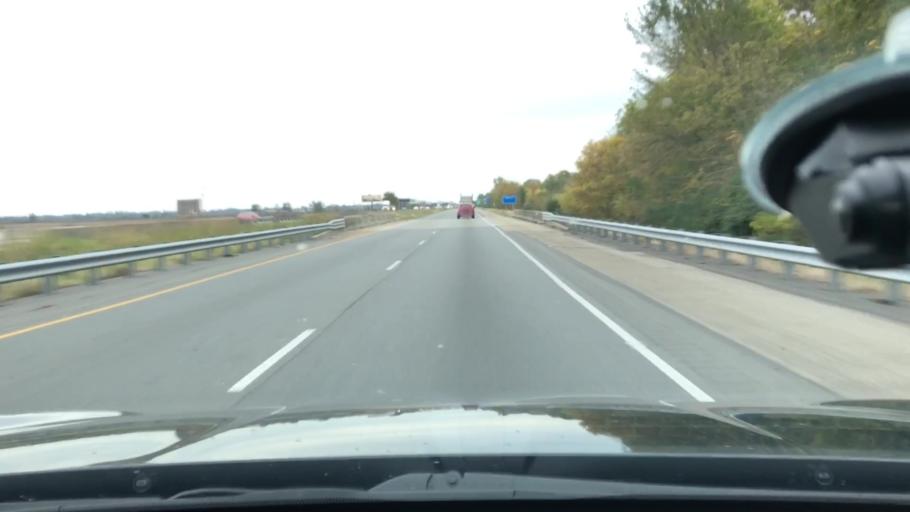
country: US
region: Arkansas
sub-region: Miller County
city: Texarkana
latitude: 33.4936
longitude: -93.9662
